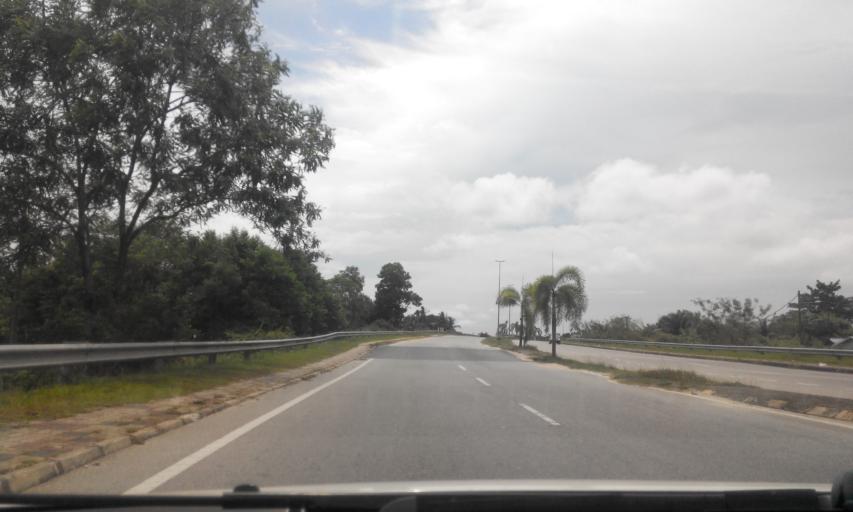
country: MY
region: Perak
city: Parit Buntar
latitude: 5.1276
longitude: 100.5076
